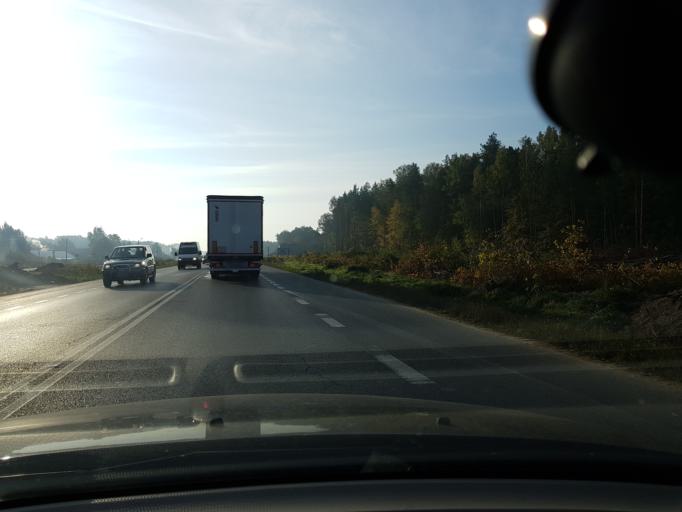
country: PL
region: Masovian Voivodeship
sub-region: Powiat otwocki
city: Otwock
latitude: 52.1615
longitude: 21.3028
